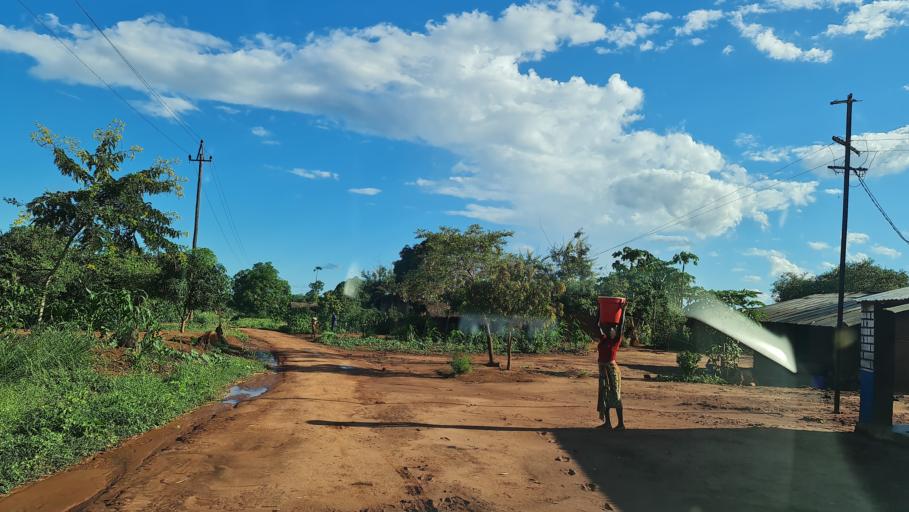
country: MZ
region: Nampula
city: Ilha de Mocambique
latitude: -14.9184
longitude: 40.2172
